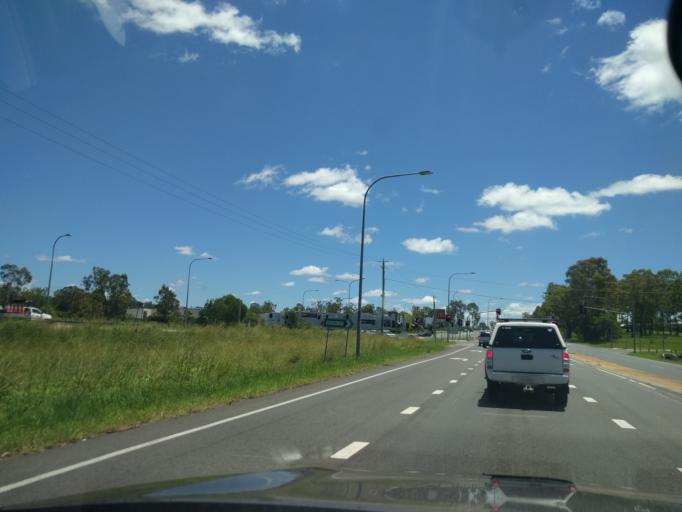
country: AU
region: Queensland
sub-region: Logan
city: Cedar Vale
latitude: -27.8355
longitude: 153.0269
